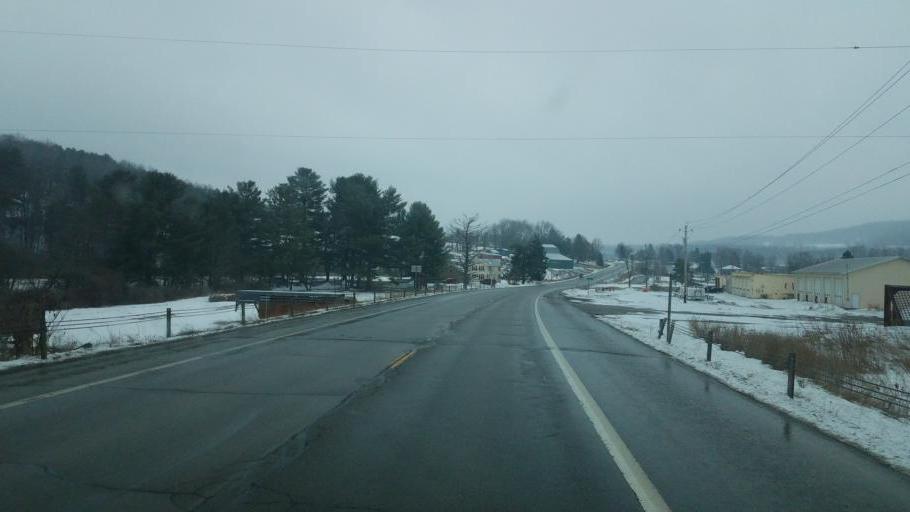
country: US
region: Pennsylvania
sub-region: Tioga County
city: Elkland
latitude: 42.0872
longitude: -77.4132
